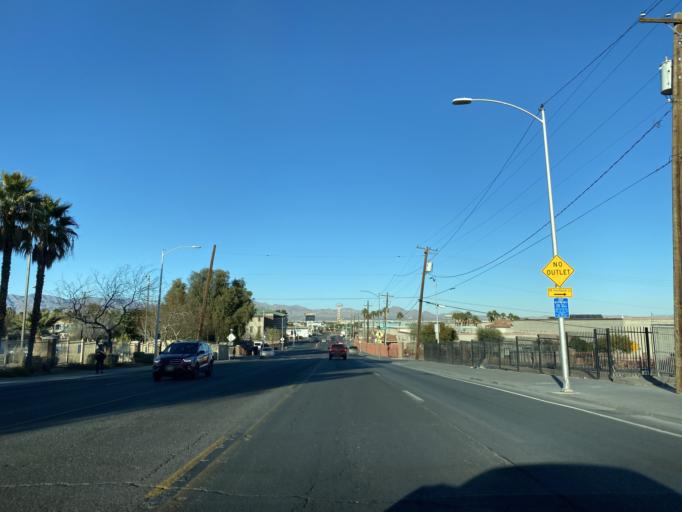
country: US
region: Nevada
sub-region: Clark County
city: Las Vegas
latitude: 36.1863
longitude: -115.1368
